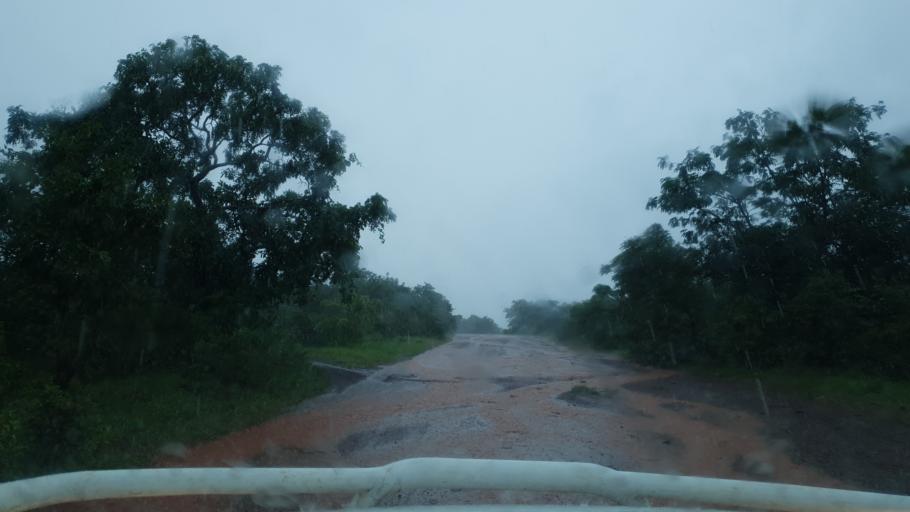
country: ML
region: Sikasso
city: Kolondieba
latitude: 11.6192
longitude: -6.6794
